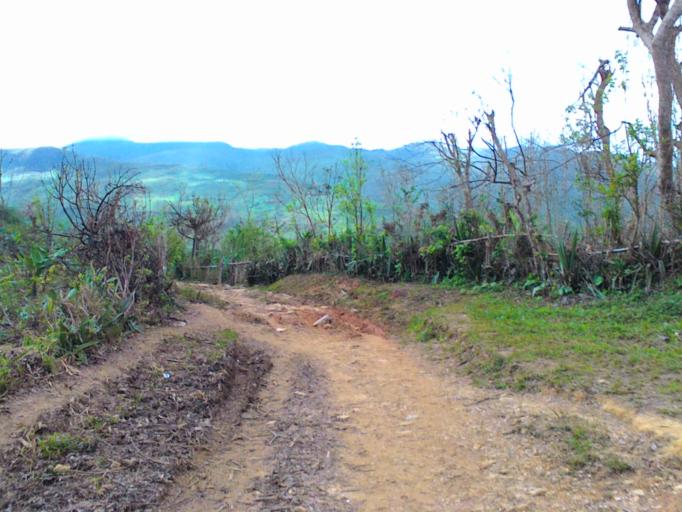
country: HT
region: Grandans
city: Moron
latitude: 18.4569
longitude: -74.1156
